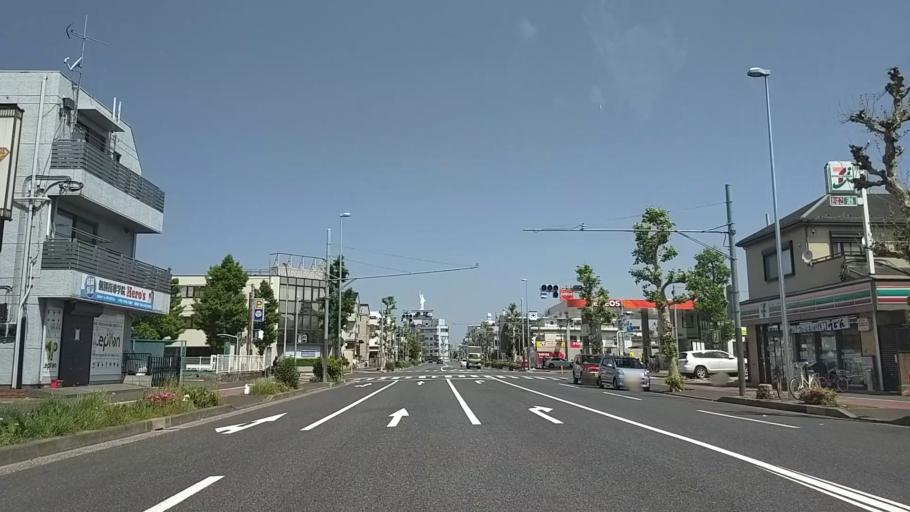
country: JP
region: Kanagawa
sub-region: Kawasaki-shi
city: Kawasaki
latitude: 35.5144
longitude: 139.6905
